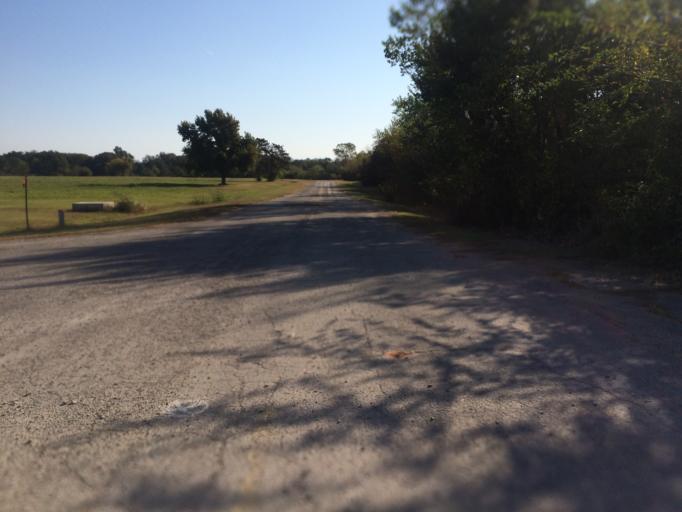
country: US
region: Oklahoma
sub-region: Cleveland County
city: Norman
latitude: 35.1809
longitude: -97.4357
